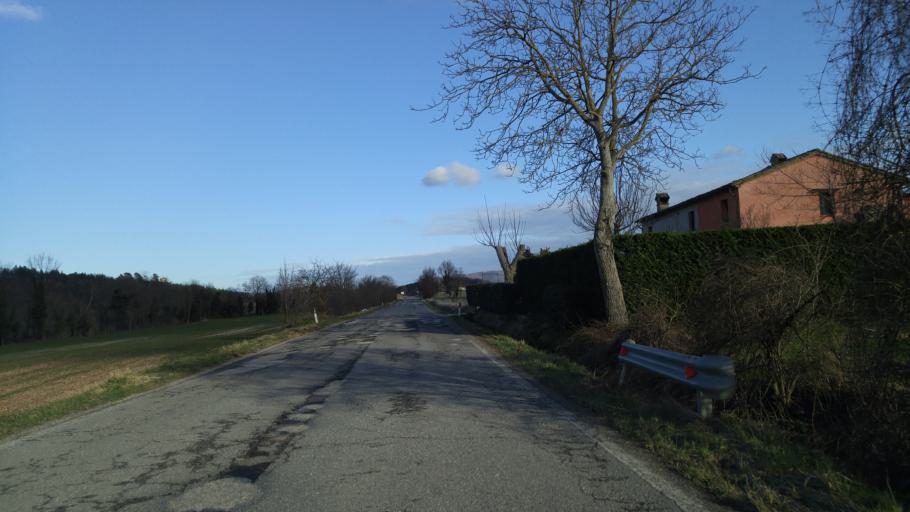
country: IT
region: The Marches
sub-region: Provincia di Pesaro e Urbino
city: Cagli
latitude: 43.5401
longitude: 12.6833
